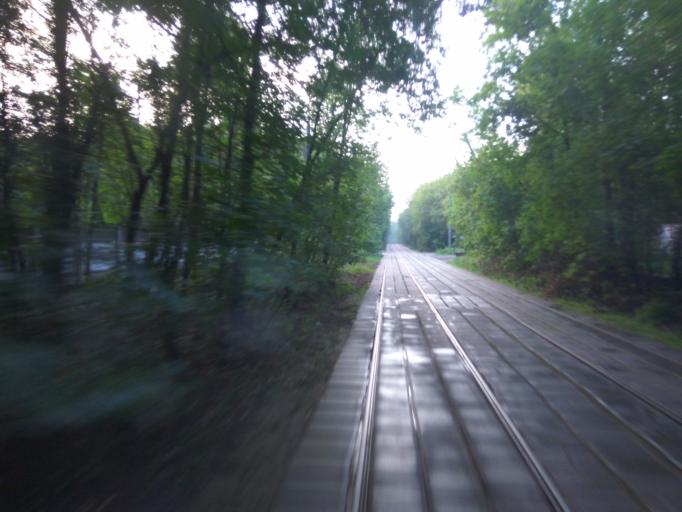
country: RU
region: Moscow
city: Sokol'niki
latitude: 55.8081
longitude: 37.6887
